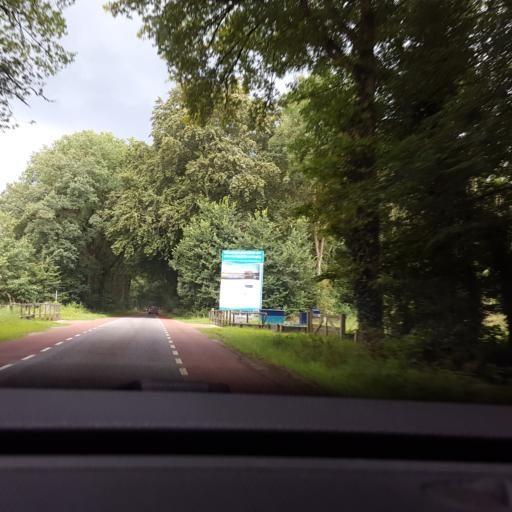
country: NL
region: Gelderland
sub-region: Gemeente Bronckhorst
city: Baak
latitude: 52.0938
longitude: 6.2751
